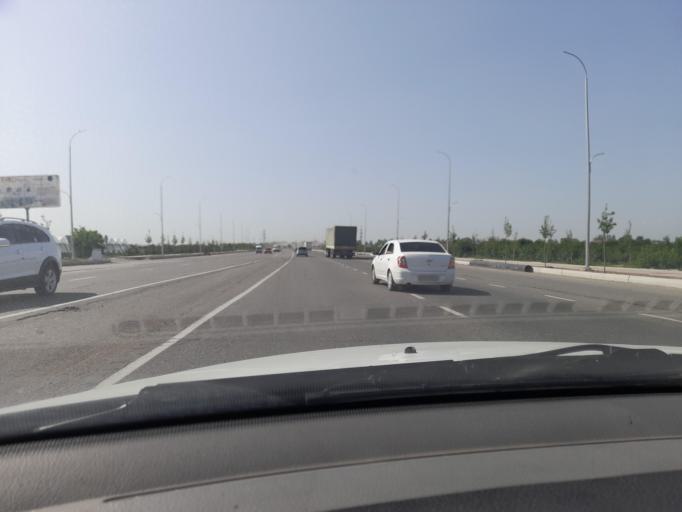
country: UZ
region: Samarqand
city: Daxbet
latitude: 39.7362
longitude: 66.9320
